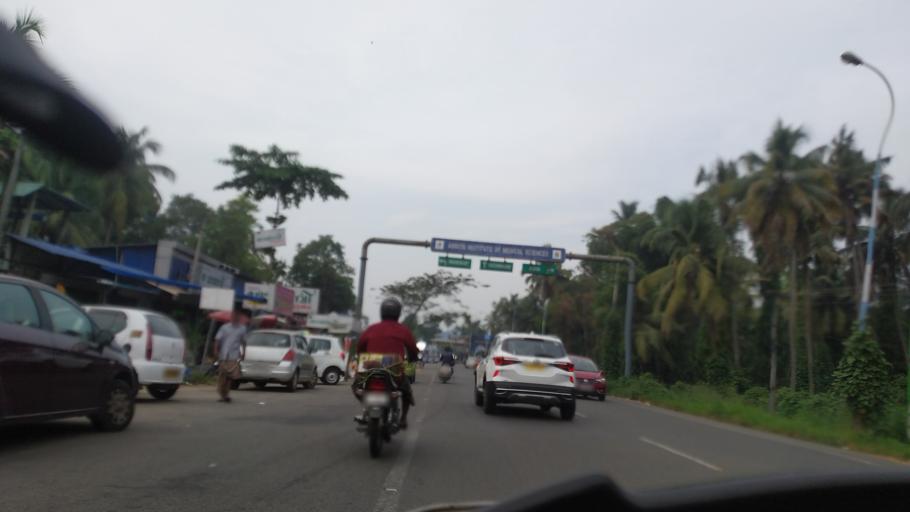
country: IN
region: Kerala
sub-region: Ernakulam
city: Elur
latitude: 10.0439
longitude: 76.2986
